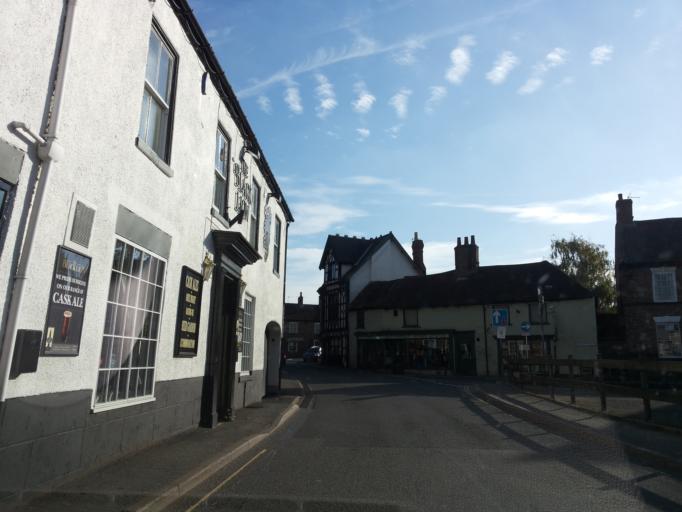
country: GB
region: England
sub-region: East Riding of Yorkshire
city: Snaith
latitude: 53.6920
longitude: -1.0284
